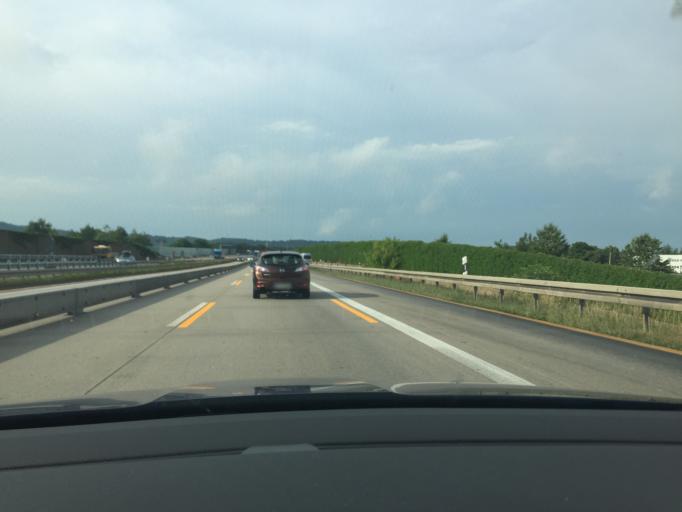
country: DE
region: Saxony
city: Radebeul
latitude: 51.0858
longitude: 13.6911
